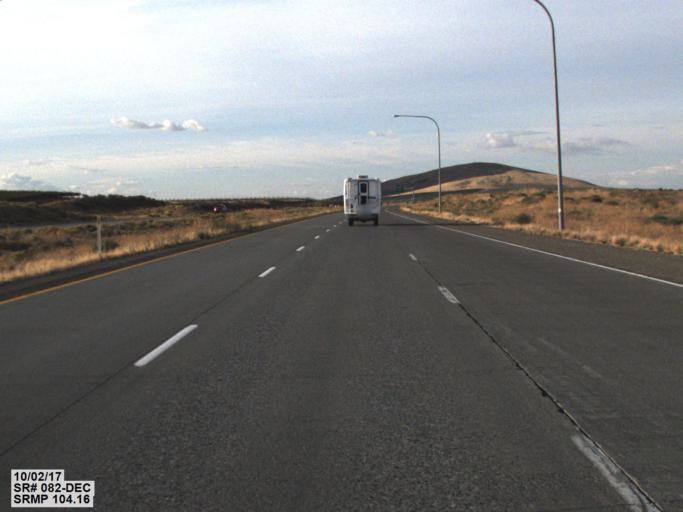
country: US
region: Washington
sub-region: Benton County
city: West Richland
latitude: 46.2221
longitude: -119.3506
